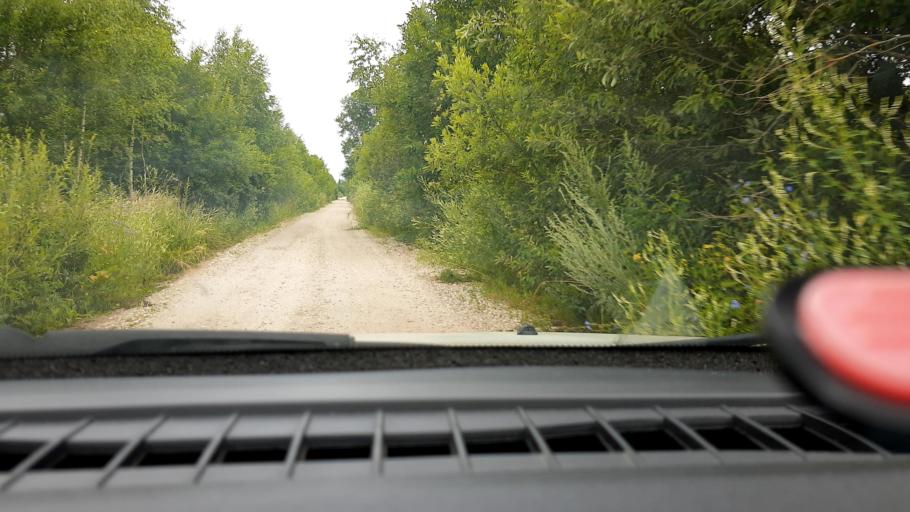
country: RU
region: Vladimir
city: Luknovo
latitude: 56.2237
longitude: 42.0292
